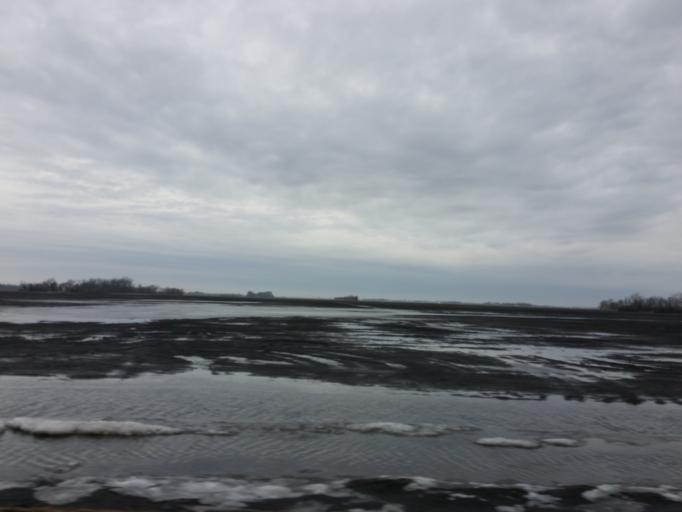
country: US
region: North Dakota
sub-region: Walsh County
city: Grafton
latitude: 48.3936
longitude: -97.4704
